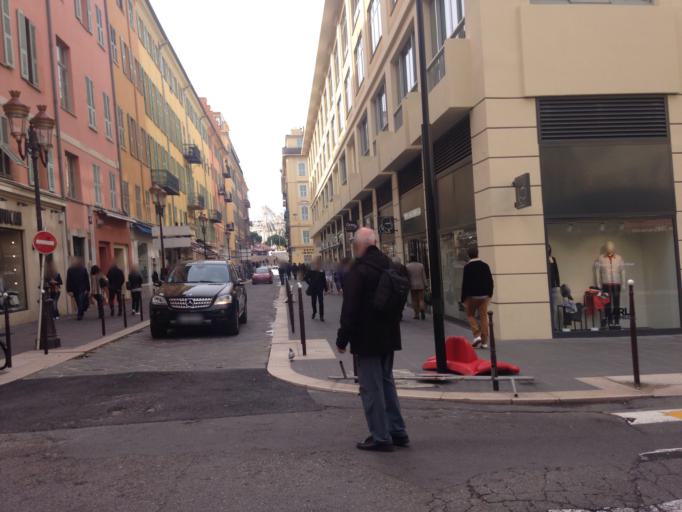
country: FR
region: Provence-Alpes-Cote d'Azur
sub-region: Departement des Alpes-Maritimes
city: Nice
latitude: 43.6964
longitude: 7.2730
